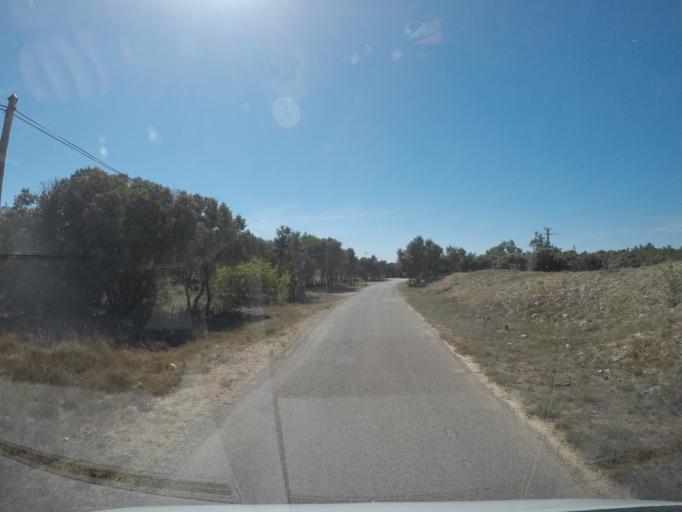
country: FR
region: Languedoc-Roussillon
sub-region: Departement de l'Herault
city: Aniane
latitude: 43.7287
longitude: 3.6491
